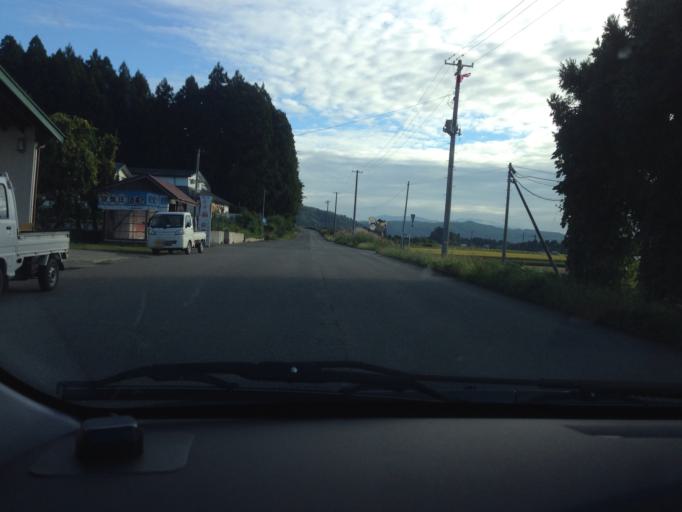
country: JP
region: Fukushima
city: Kitakata
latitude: 37.5939
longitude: 139.7733
